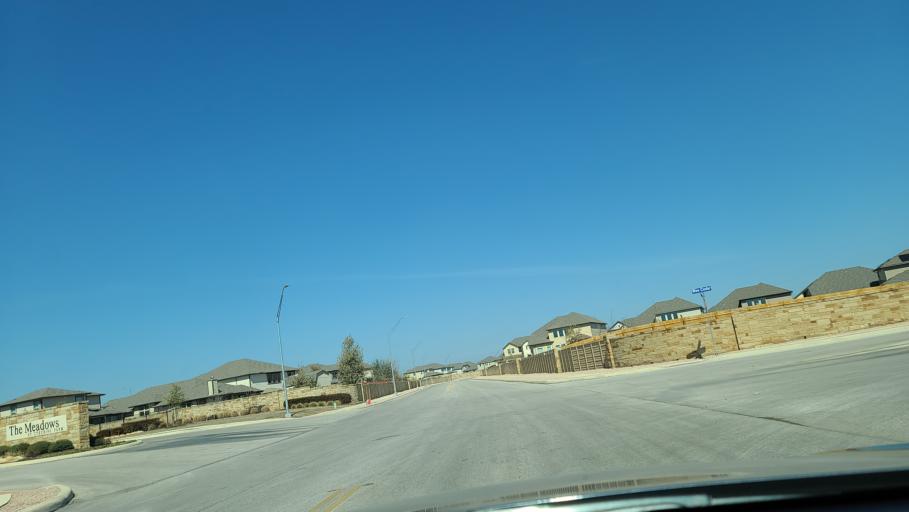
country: US
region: Texas
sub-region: Bexar County
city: Leon Valley
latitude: 29.5592
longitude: -98.6202
